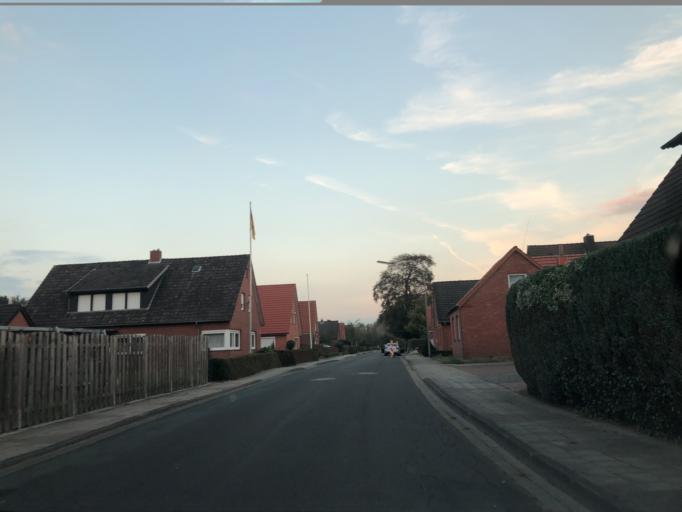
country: DE
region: Lower Saxony
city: Papenburg
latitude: 53.0716
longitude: 7.4285
